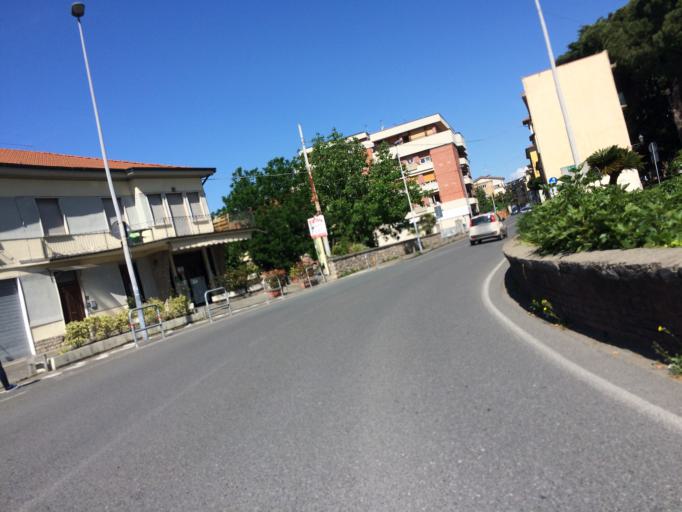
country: IT
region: Liguria
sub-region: Provincia di La Spezia
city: Sarzana
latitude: 44.1102
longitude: 9.9635
